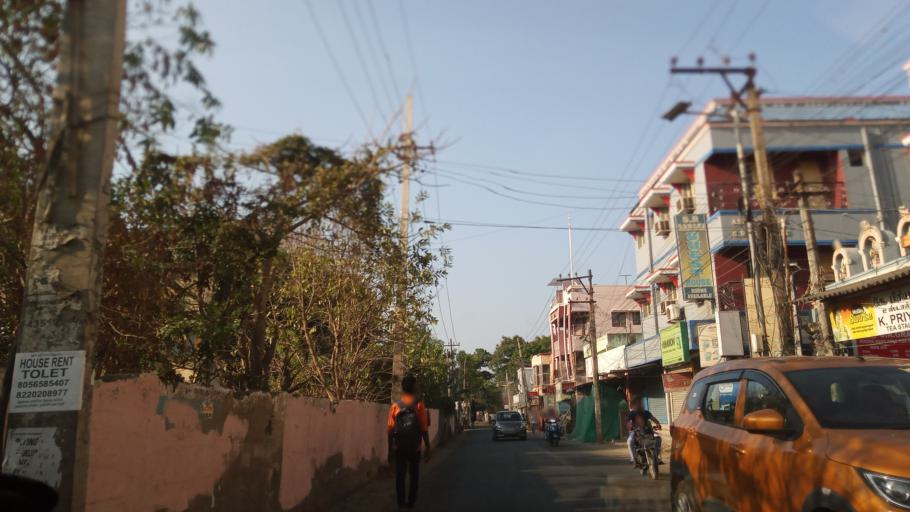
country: IN
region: Tamil Nadu
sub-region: Kancheepuram
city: Manappakkam
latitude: 13.0227
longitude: 80.1837
